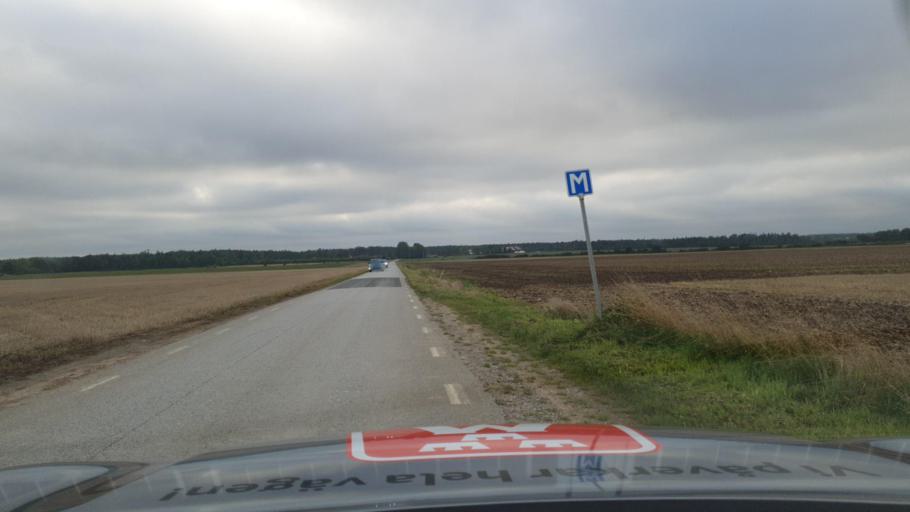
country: SE
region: Gotland
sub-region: Gotland
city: Visby
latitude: 57.5332
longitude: 18.4156
